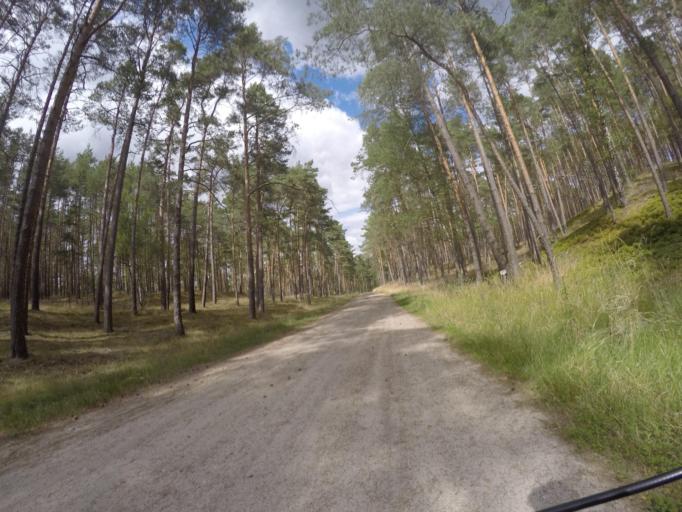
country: DE
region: Lower Saxony
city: Neu Darchau
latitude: 53.2609
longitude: 10.9777
